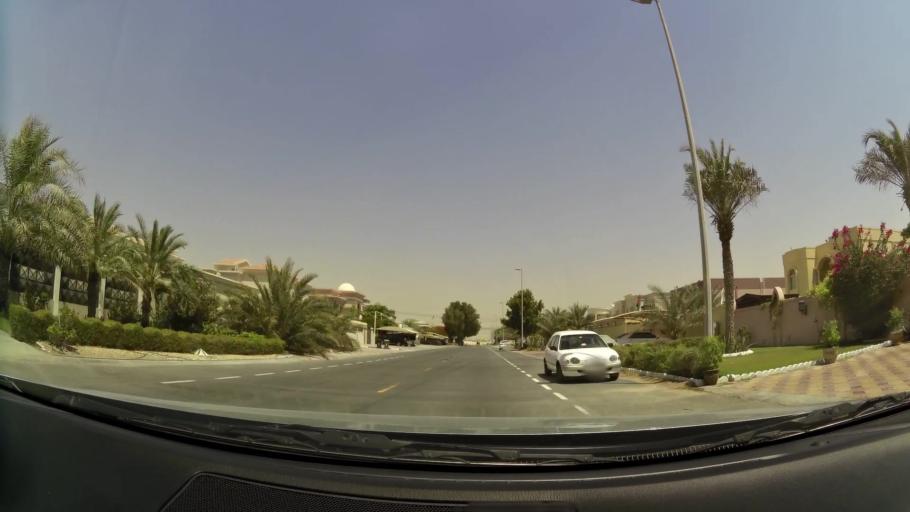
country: AE
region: Dubai
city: Dubai
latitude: 25.0937
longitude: 55.2162
